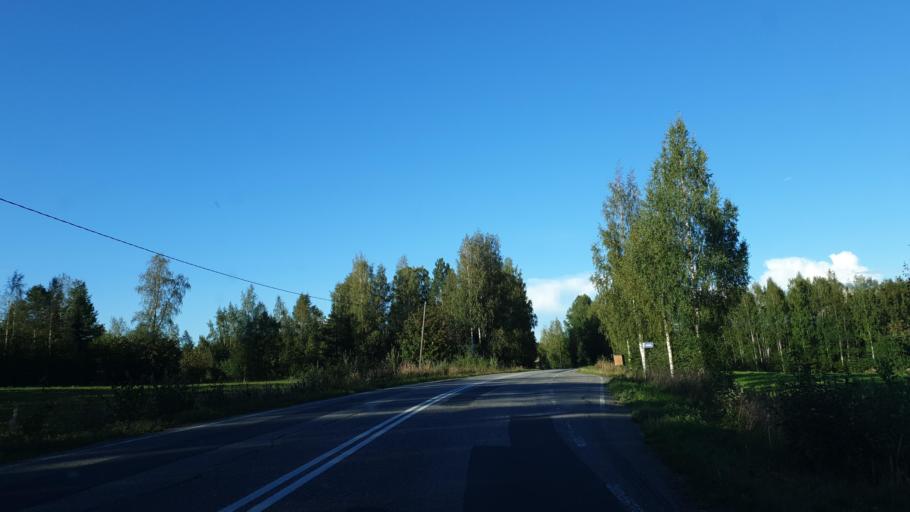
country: FI
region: Northern Savo
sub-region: Koillis-Savo
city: Juankoski
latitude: 63.1110
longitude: 28.4447
